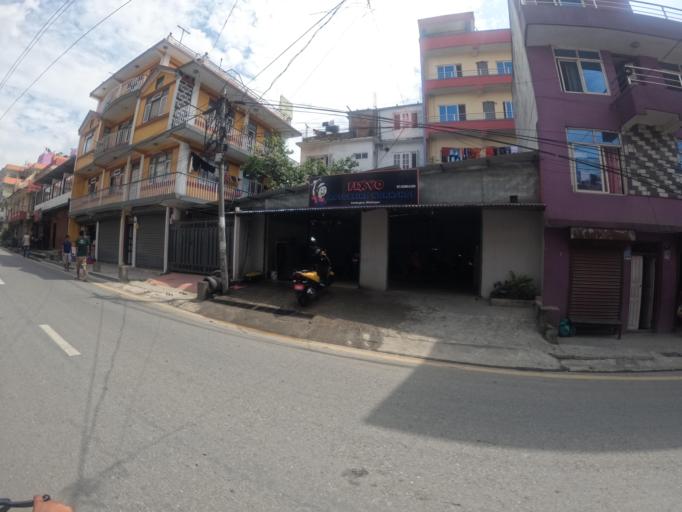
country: NP
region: Central Region
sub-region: Bagmati Zone
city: Bhaktapur
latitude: 27.6787
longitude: 85.3758
